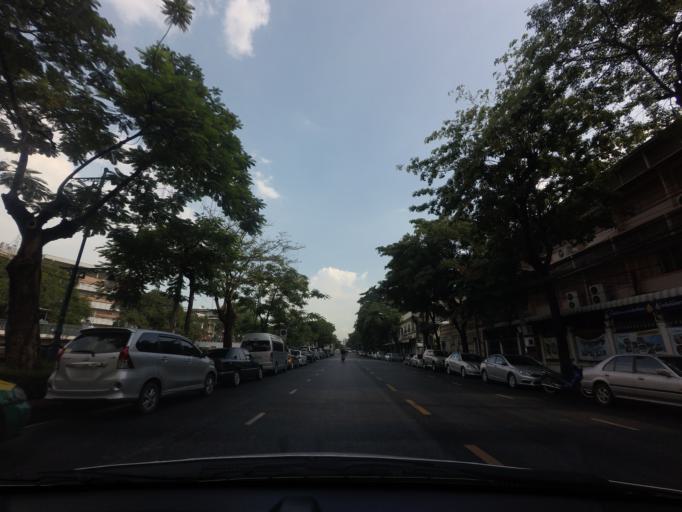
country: TH
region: Bangkok
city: Pom Prap Sattru Phai
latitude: 13.7611
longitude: 100.5117
